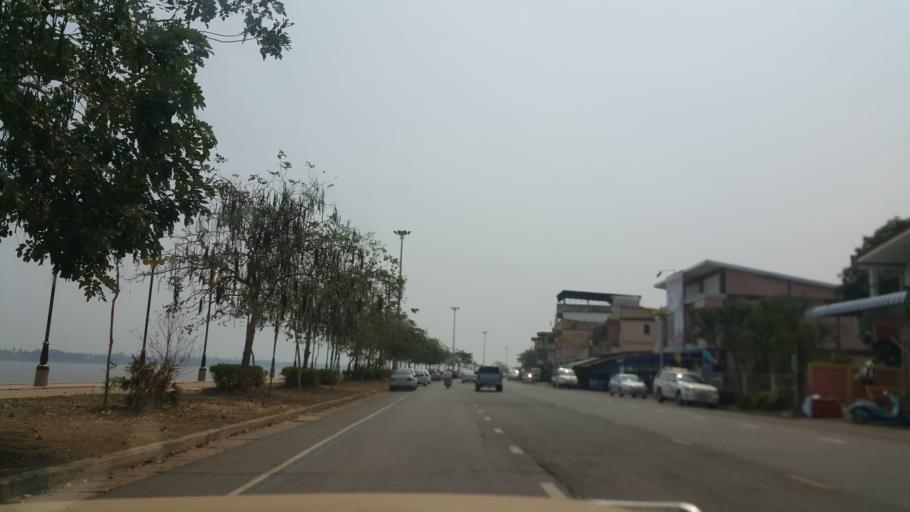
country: TH
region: Nakhon Phanom
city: Nakhon Phanom
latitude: 17.3971
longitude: 104.7912
